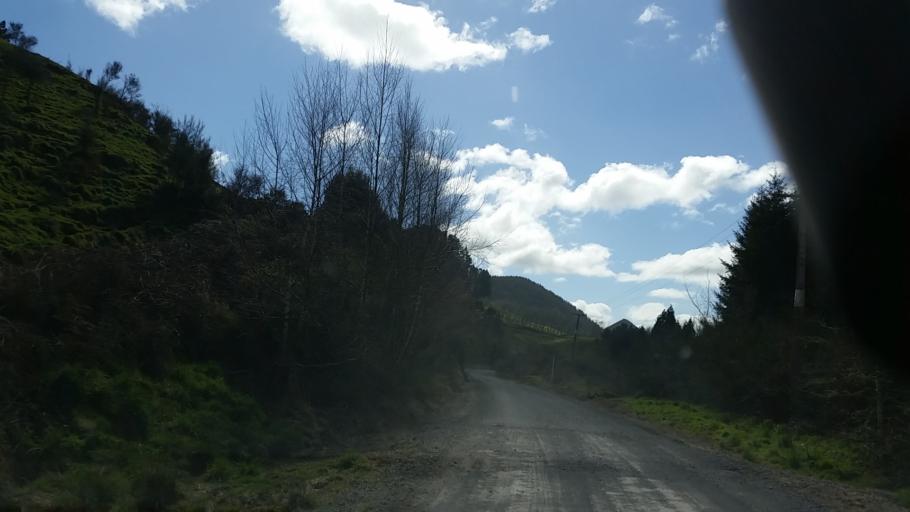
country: NZ
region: Waikato
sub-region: Taupo District
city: Taupo
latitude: -38.4731
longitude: 176.2247
